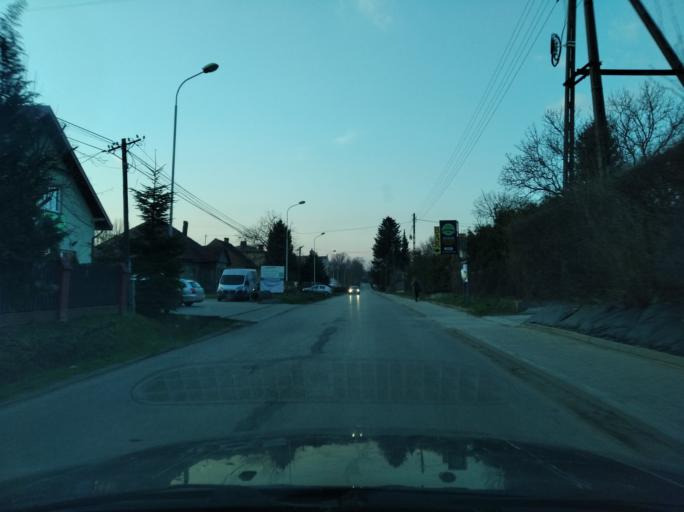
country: PL
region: Subcarpathian Voivodeship
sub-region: Powiat przeworski
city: Przeworsk
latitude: 50.0512
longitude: 22.5014
